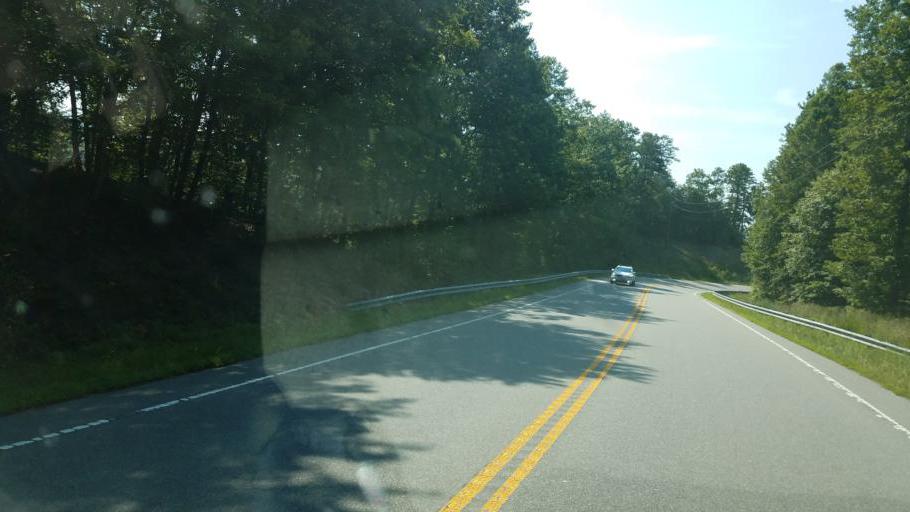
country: US
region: North Carolina
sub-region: Burke County
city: Glen Alpine
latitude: 35.9088
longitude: -81.8076
